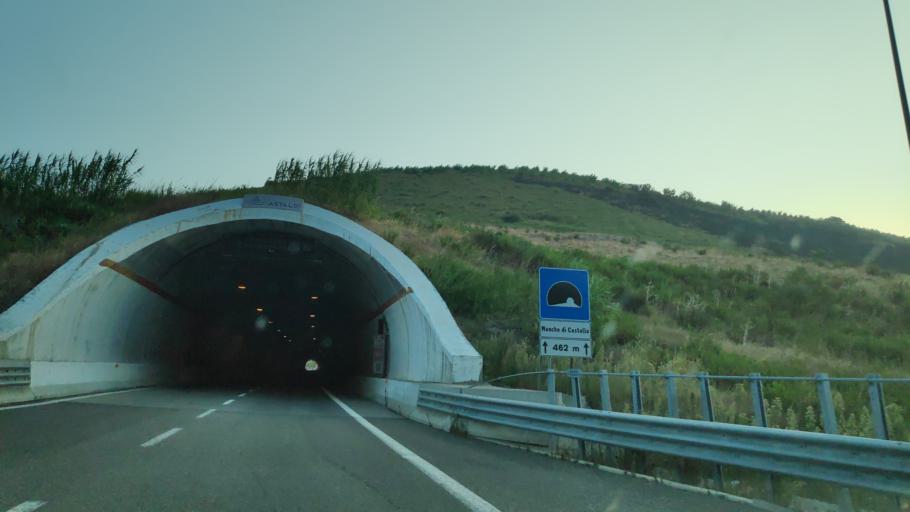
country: IT
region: Calabria
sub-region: Provincia di Catanzaro
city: Squillace Lido
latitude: 38.7985
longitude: 16.5517
